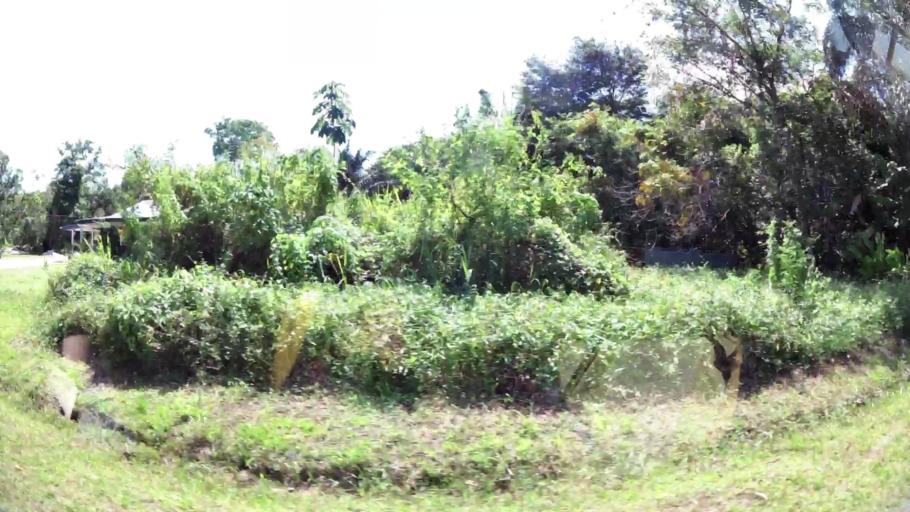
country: GF
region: Guyane
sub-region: Guyane
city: Matoury
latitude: 4.8445
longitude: -52.3295
